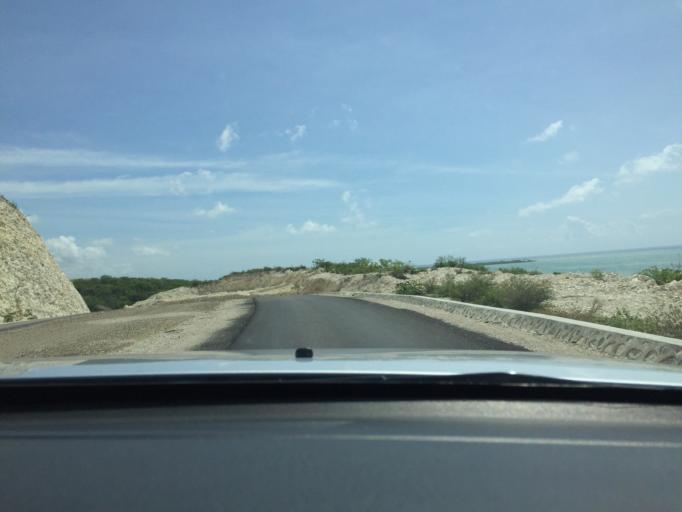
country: HT
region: Sud
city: Aquin
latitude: 18.2358
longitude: -73.2867
